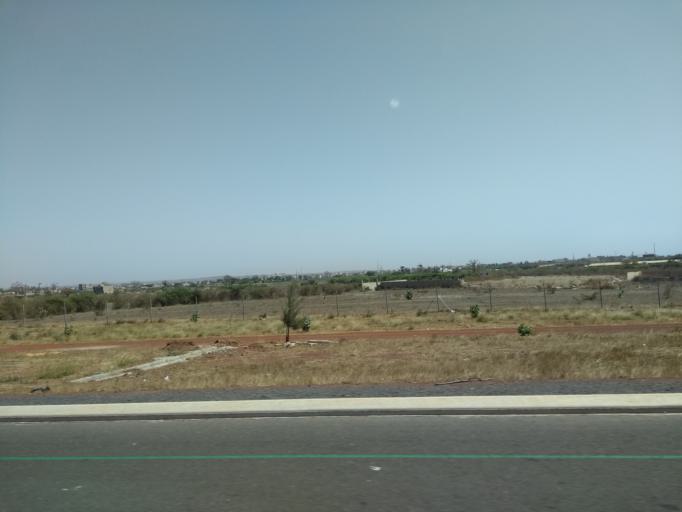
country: SN
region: Thies
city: Thies
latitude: 14.7385
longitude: -17.1926
